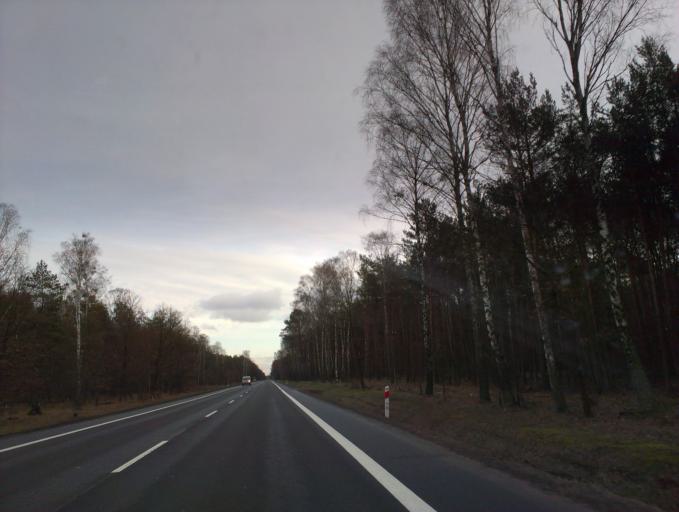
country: PL
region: Masovian Voivodeship
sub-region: Powiat sierpecki
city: Sierpc
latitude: 52.8748
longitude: 19.6118
